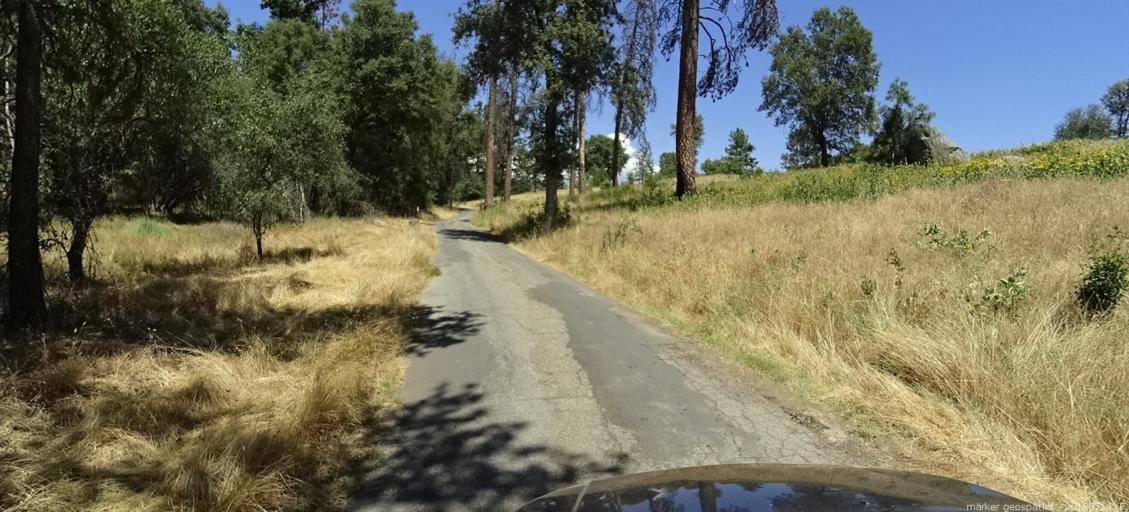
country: US
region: California
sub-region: Madera County
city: Ahwahnee
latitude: 37.3958
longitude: -119.7473
